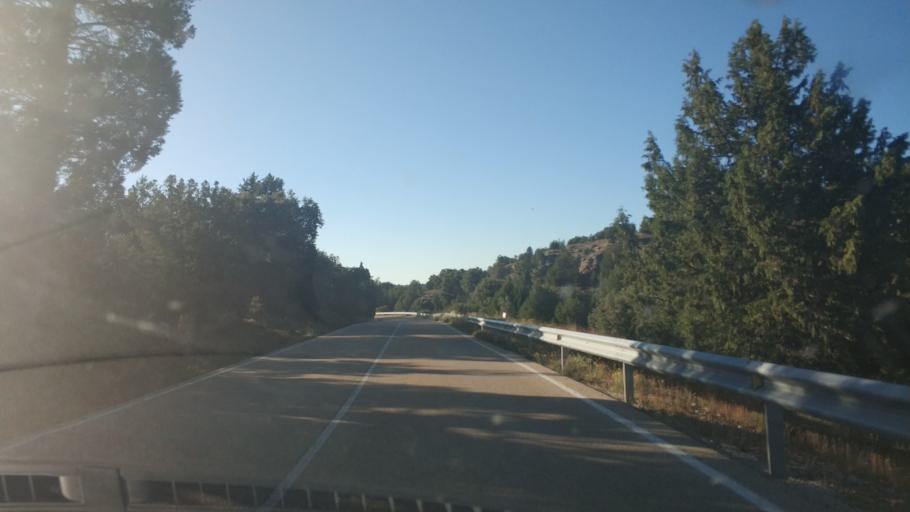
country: ES
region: Castille and Leon
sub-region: Provincia de Soria
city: Montejo de Tiermes
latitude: 41.4253
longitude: -3.2018
